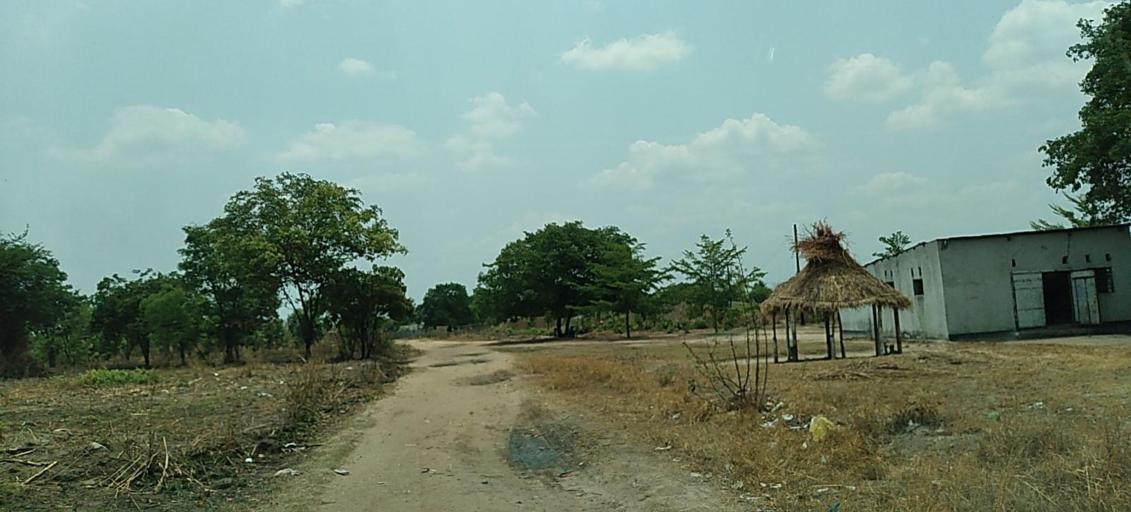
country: ZM
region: Copperbelt
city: Luanshya
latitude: -13.1005
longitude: 28.3028
